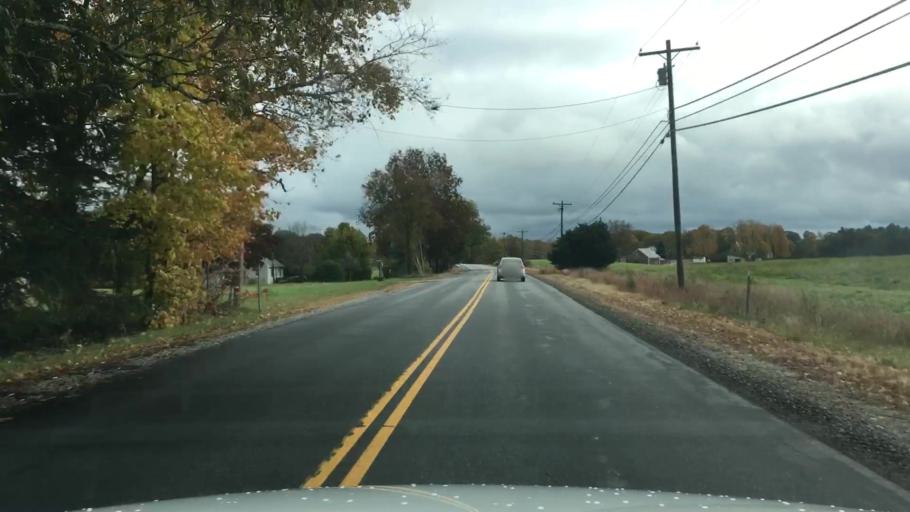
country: US
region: New Hampshire
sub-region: Strafford County
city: Lee
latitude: 43.1066
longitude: -70.9943
